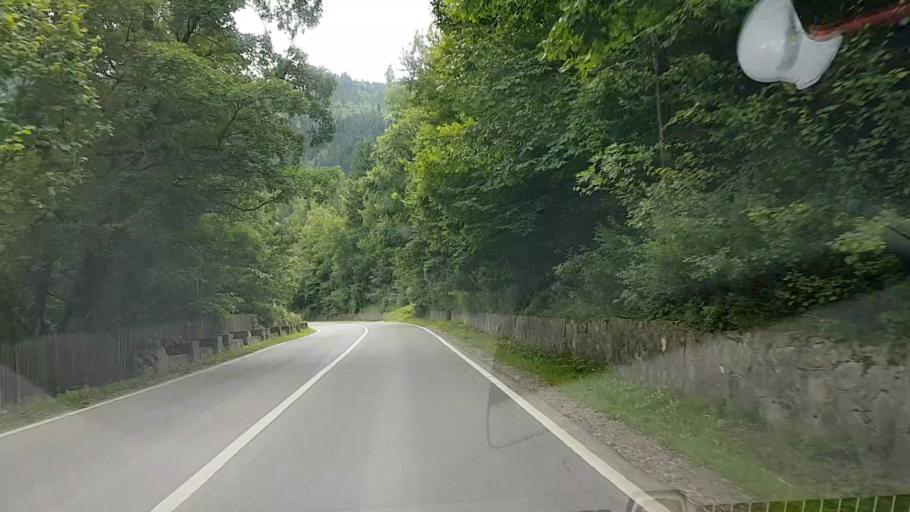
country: RO
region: Neamt
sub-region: Comuna Poiana Teiului
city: Poiana Teiului
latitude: 47.0983
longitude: 25.9417
